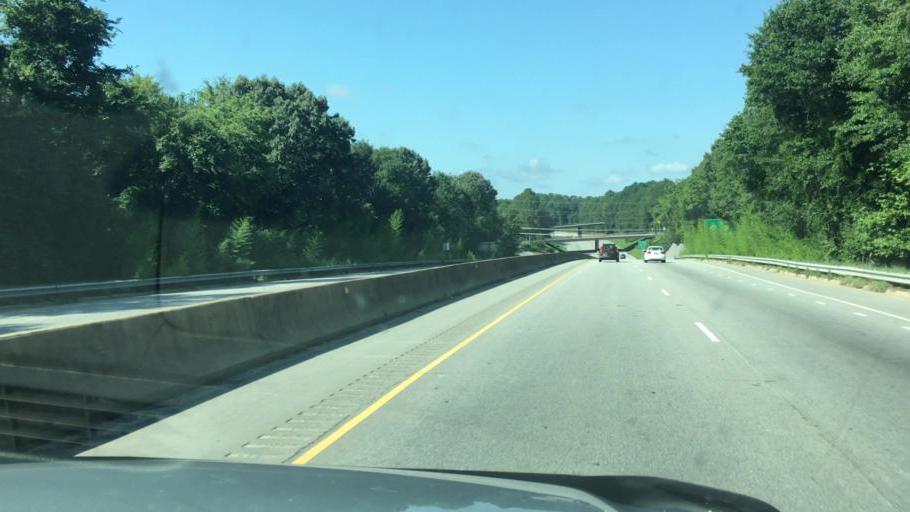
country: US
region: North Carolina
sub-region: Cumberland County
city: Fayetteville
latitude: 35.0685
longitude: -78.8825
